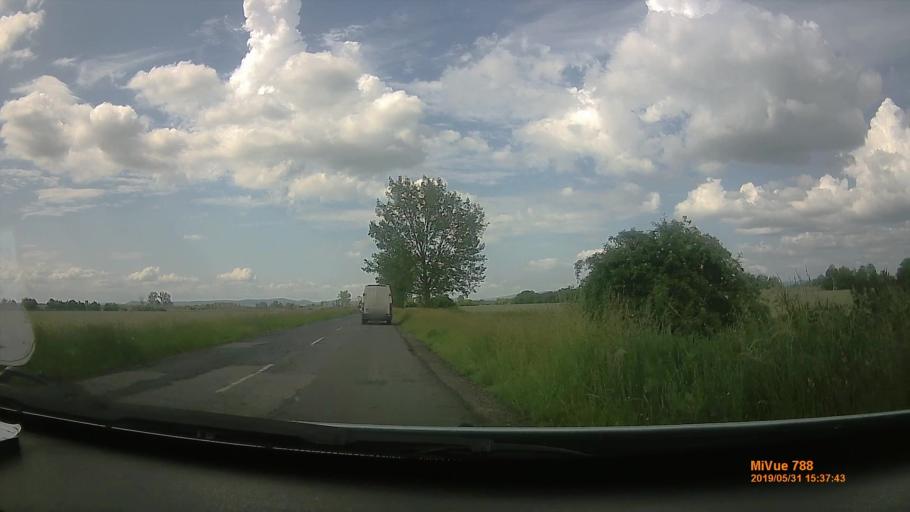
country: HU
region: Borsod-Abauj-Zemplen
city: Prugy
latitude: 48.0944
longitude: 21.2412
